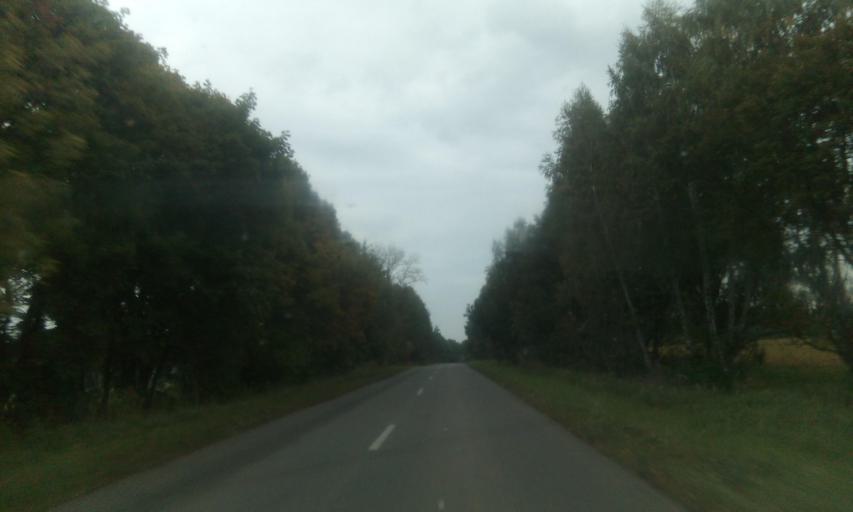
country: RU
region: Tula
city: Dubovka
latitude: 53.9597
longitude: 38.0794
